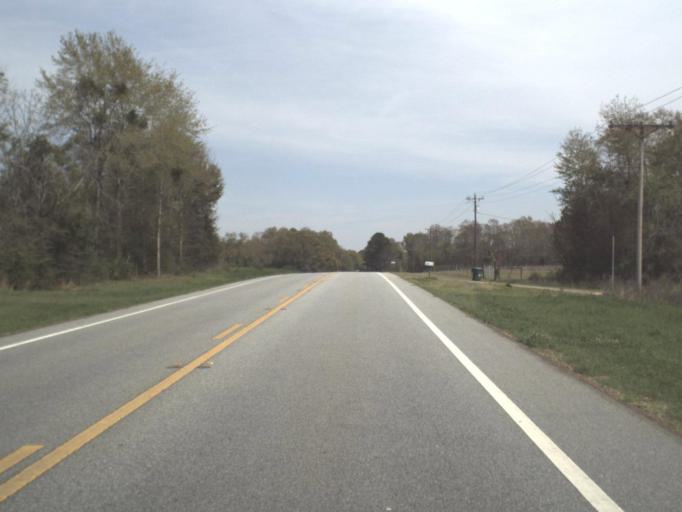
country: US
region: Alabama
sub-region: Geneva County
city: Geneva
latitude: 30.9476
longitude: -85.7513
